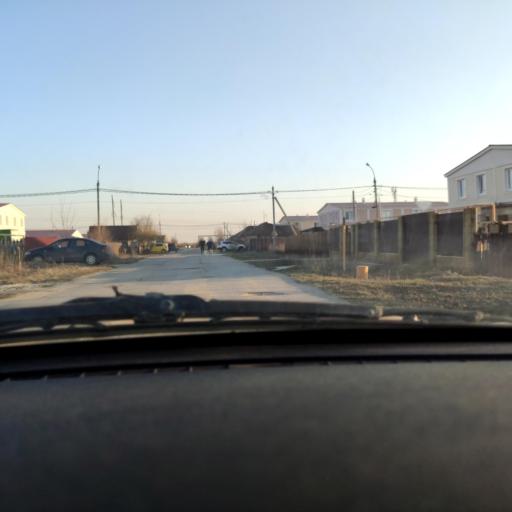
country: RU
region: Samara
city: Podstepki
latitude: 53.5711
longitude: 49.1190
